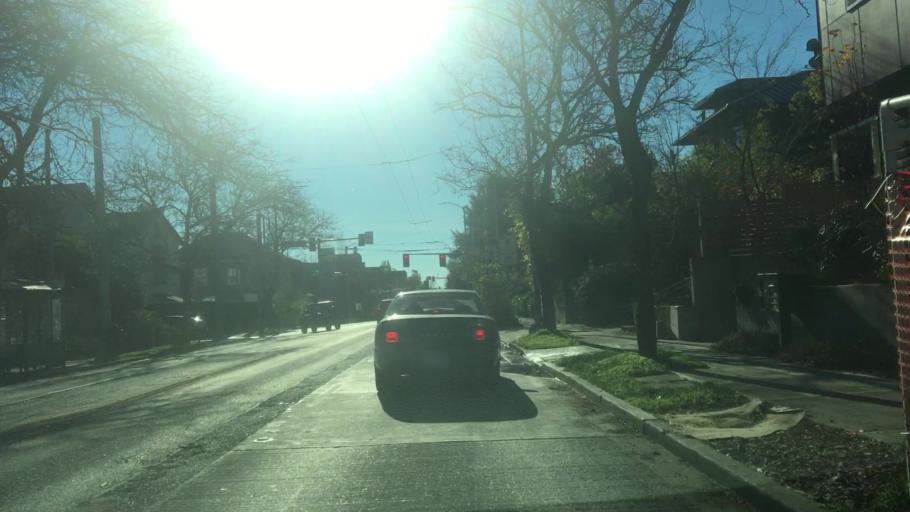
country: US
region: Washington
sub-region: King County
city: Seattle
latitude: 47.6210
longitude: -122.3026
